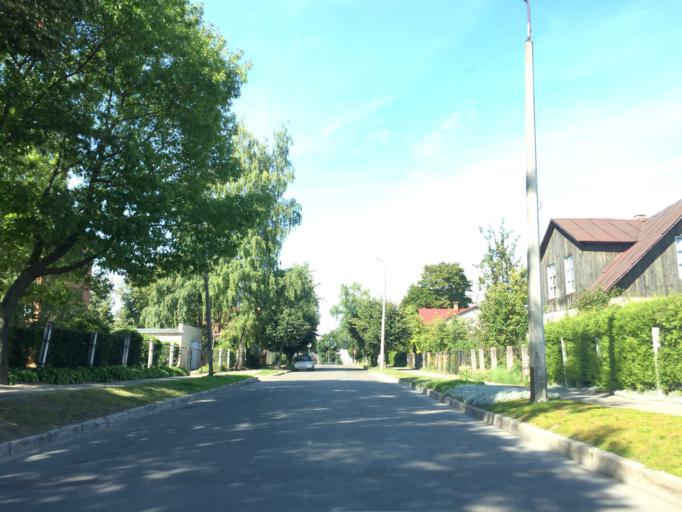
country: LV
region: Rezekne
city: Rezekne
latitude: 56.5154
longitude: 27.3417
